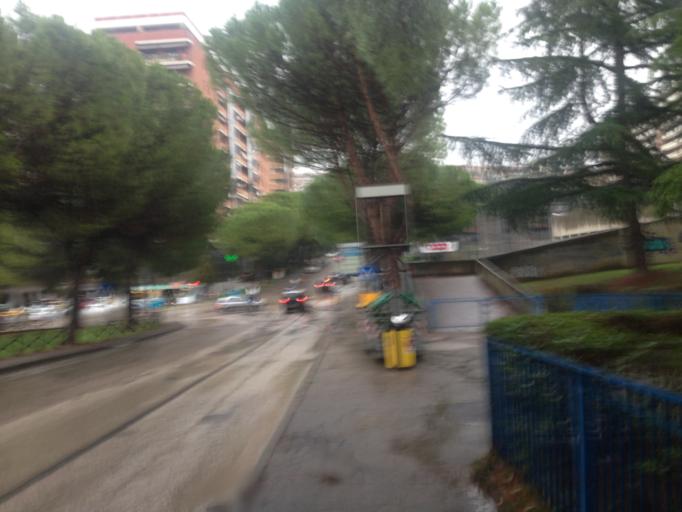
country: IT
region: Umbria
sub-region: Provincia di Perugia
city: Perugia
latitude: 43.1049
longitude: 12.3683
